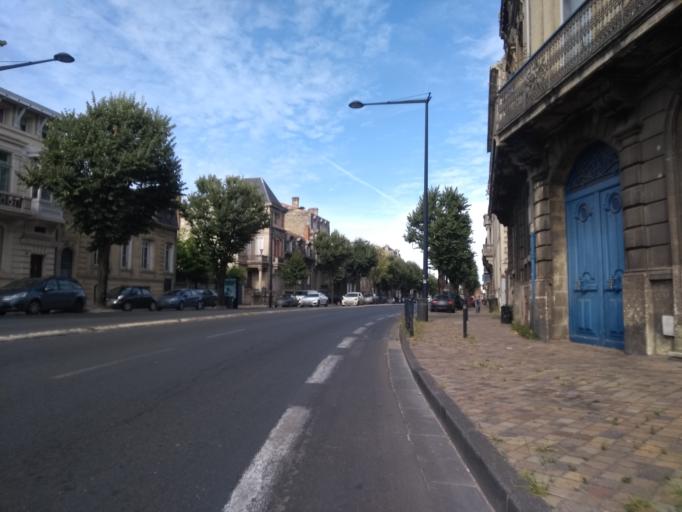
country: FR
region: Aquitaine
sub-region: Departement de la Gironde
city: Bordeaux
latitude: 44.8431
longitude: -0.5995
